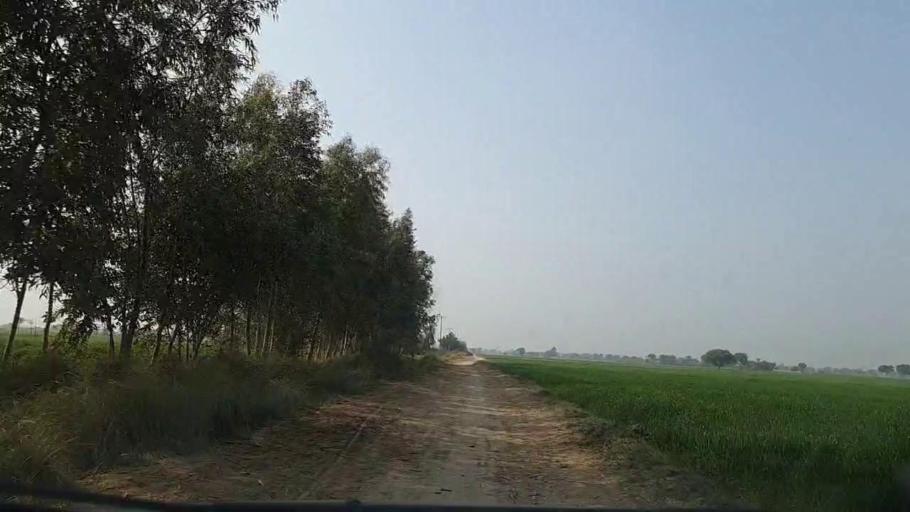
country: PK
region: Sindh
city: Sanghar
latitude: 26.0345
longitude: 68.9911
